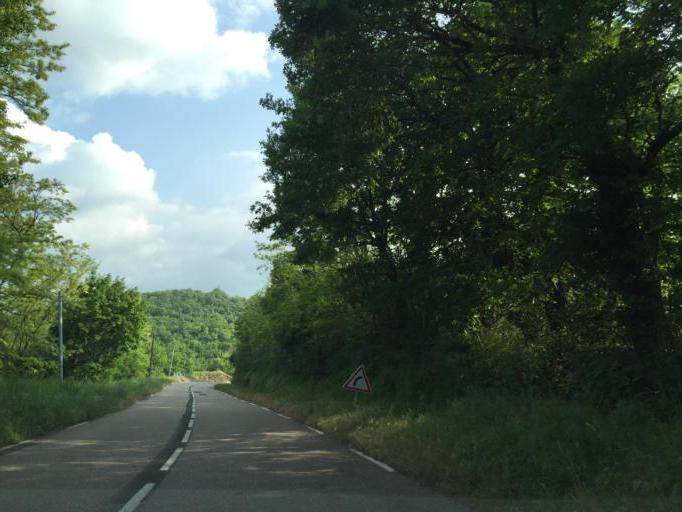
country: FR
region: Rhone-Alpes
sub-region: Departement de la Loire
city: Chateauneuf
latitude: 45.5456
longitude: 4.6660
